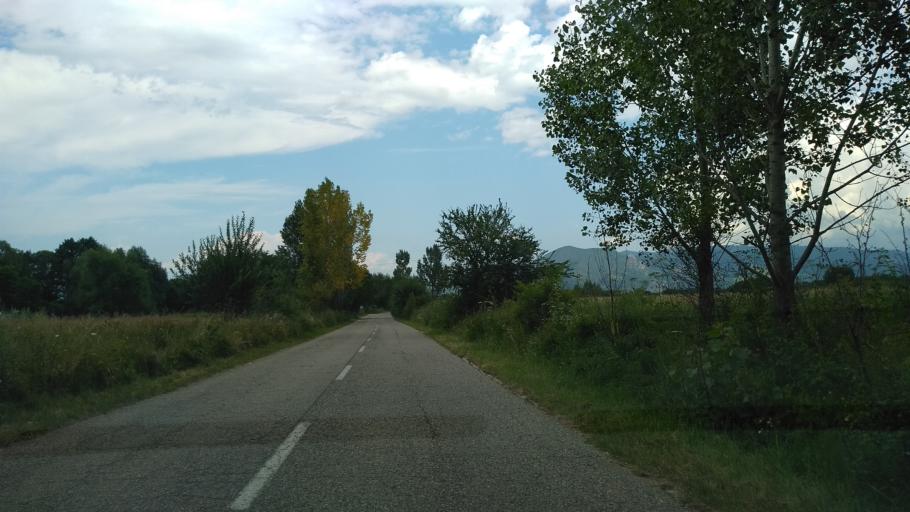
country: RO
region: Hunedoara
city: Salasu de Sus
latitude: 45.4997
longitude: 22.9481
